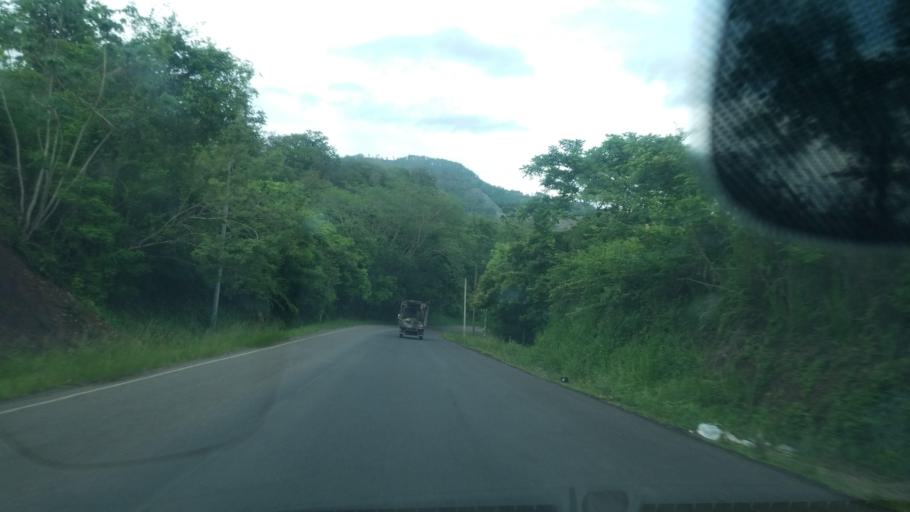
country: HN
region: Santa Barbara
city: Ceguaca
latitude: 14.8101
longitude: -88.1896
